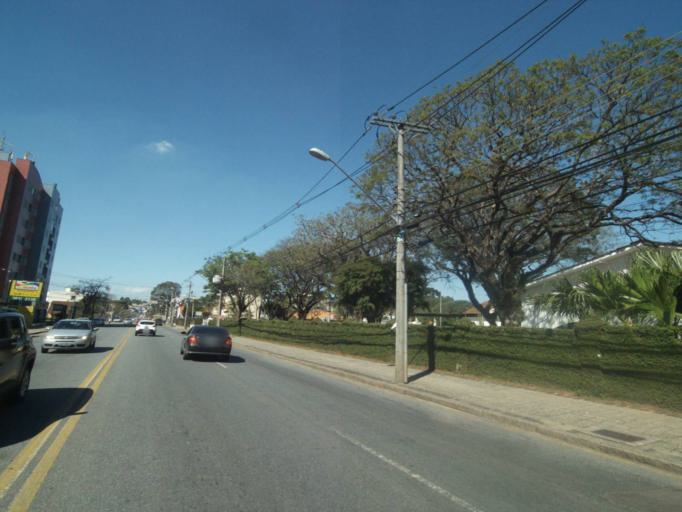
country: BR
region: Parana
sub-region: Curitiba
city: Curitiba
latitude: -25.3954
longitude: -49.2308
